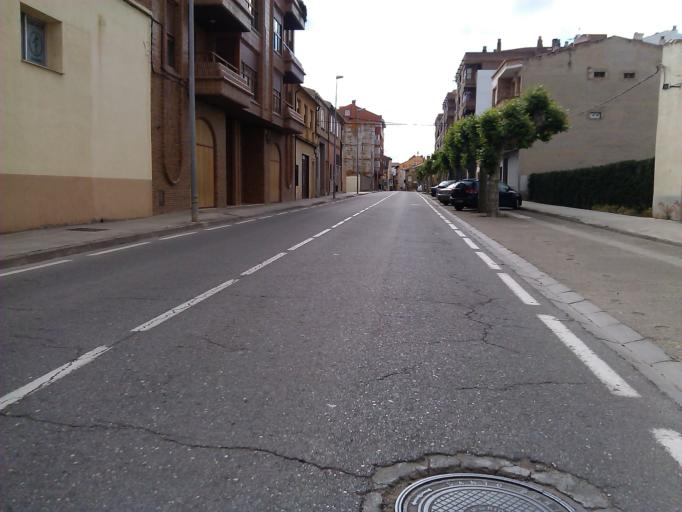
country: ES
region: La Rioja
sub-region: Provincia de La Rioja
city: Santo Domingo de la Calzada
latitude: 42.4399
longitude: -2.9471
